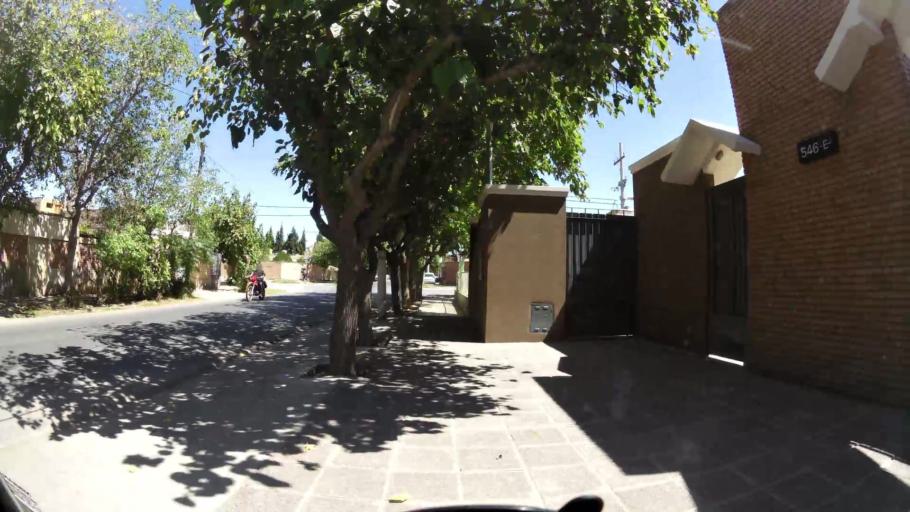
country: AR
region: San Juan
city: San Juan
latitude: -31.5230
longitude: -68.5197
